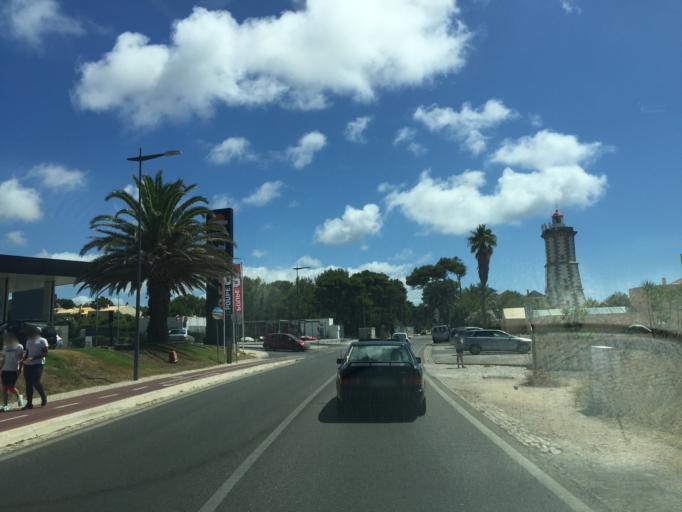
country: PT
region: Lisbon
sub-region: Cascais
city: Cascais
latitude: 38.6959
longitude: -9.4485
